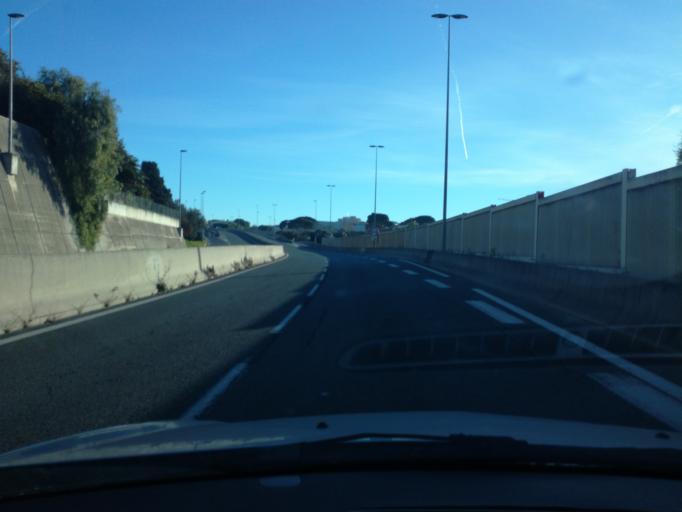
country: FR
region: Provence-Alpes-Cote d'Azur
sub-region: Departement des Alpes-Maritimes
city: Antibes
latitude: 43.5777
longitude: 7.1021
